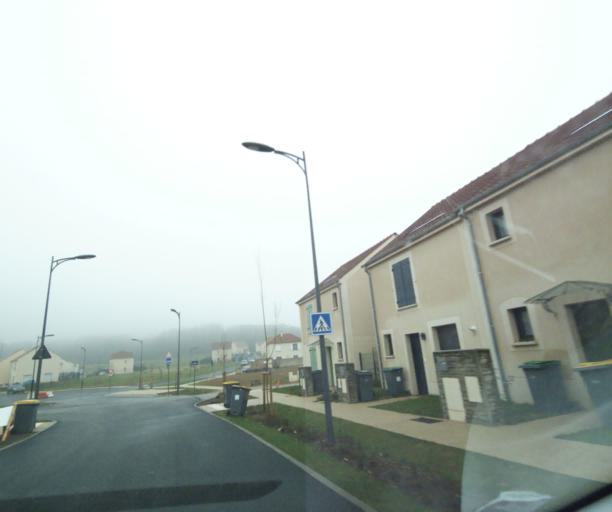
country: FR
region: Ile-de-France
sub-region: Departement de Seine-et-Marne
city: Othis
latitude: 49.0637
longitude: 2.6729
